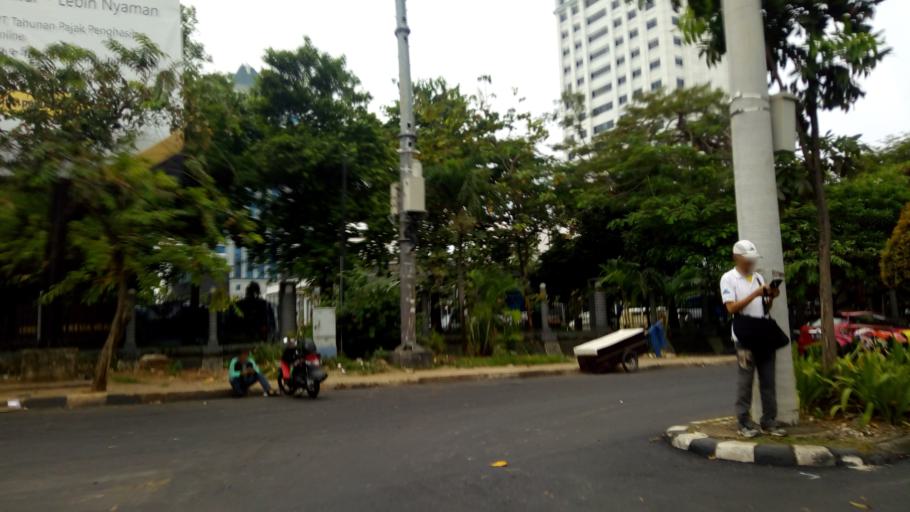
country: ID
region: Jakarta Raya
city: Jakarta
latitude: -6.1742
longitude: 106.8385
